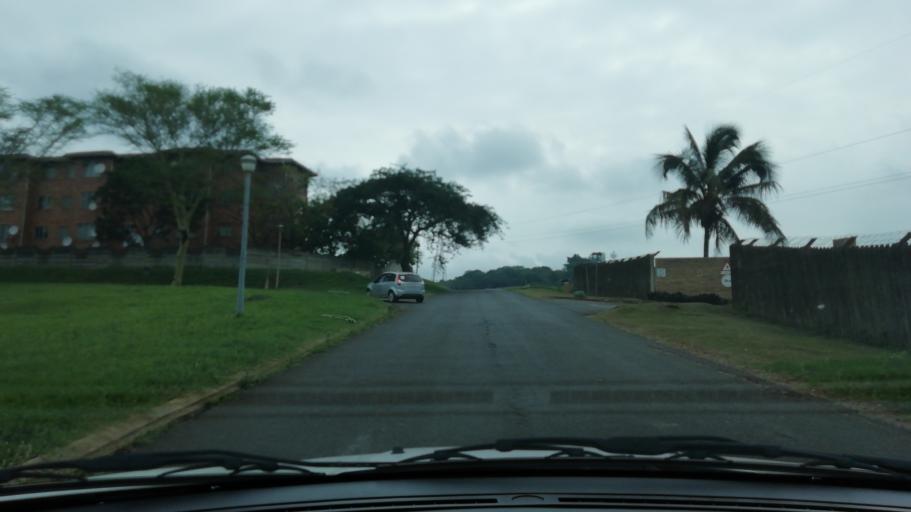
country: ZA
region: KwaZulu-Natal
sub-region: uThungulu District Municipality
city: Empangeni
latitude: -28.7391
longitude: 31.8852
